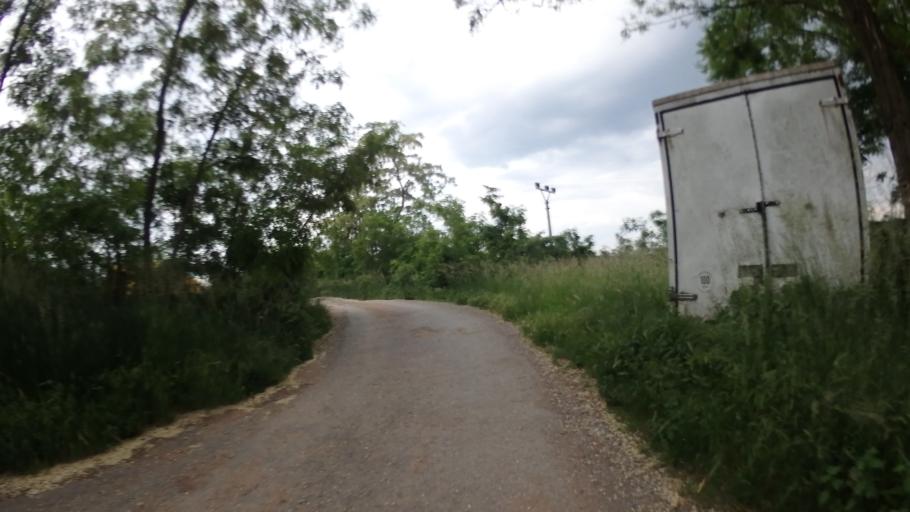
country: CZ
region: South Moravian
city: Ostopovice
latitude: 49.1339
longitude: 16.5452
